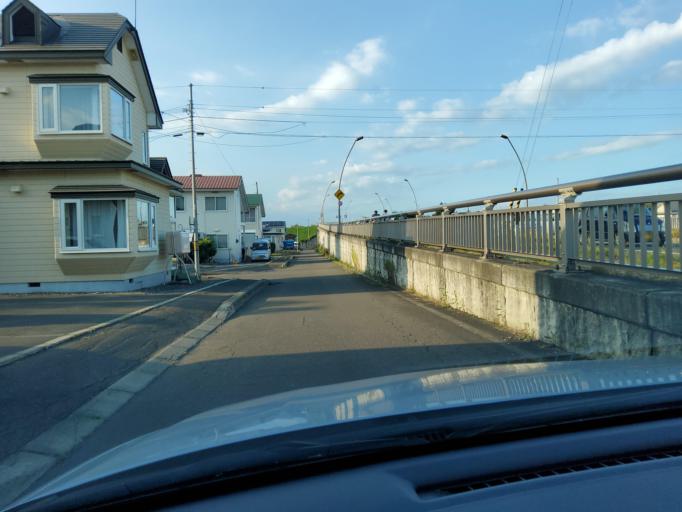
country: JP
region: Hokkaido
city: Obihiro
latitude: 42.9408
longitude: 143.1836
